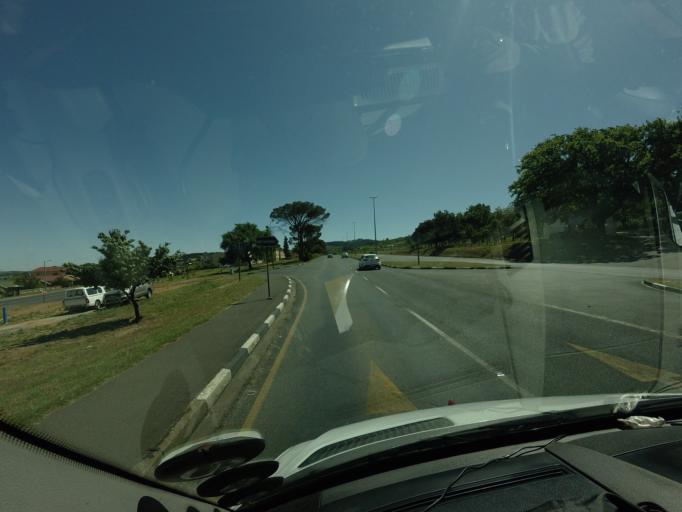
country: ZA
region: Western Cape
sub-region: Cape Winelands District Municipality
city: Stellenbosch
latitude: -33.9171
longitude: 18.8582
